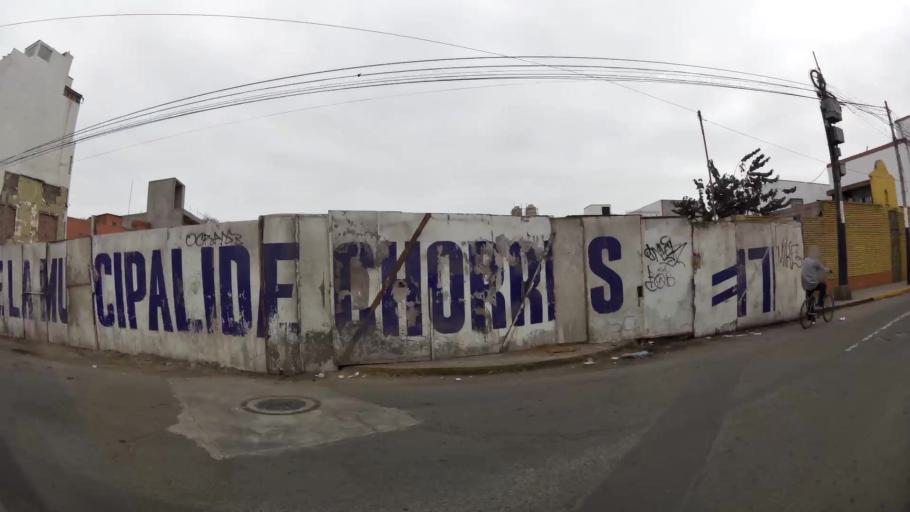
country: PE
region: Lima
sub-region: Lima
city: Surco
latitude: -12.1623
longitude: -77.0237
